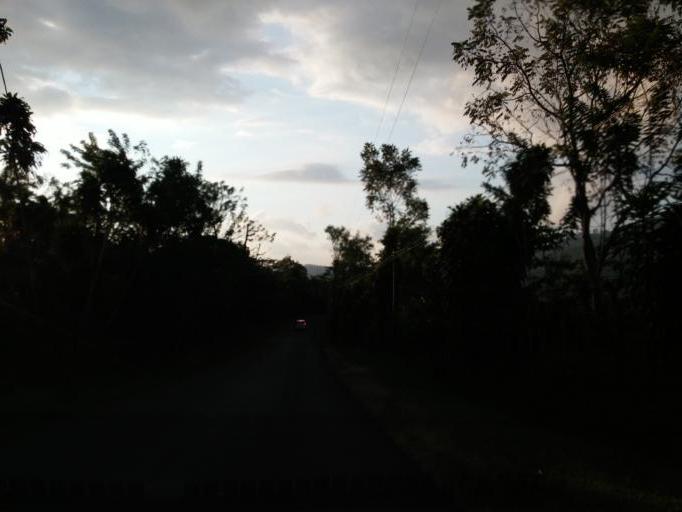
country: CR
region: San Jose
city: Palmichal
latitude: 9.8466
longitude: -84.2217
